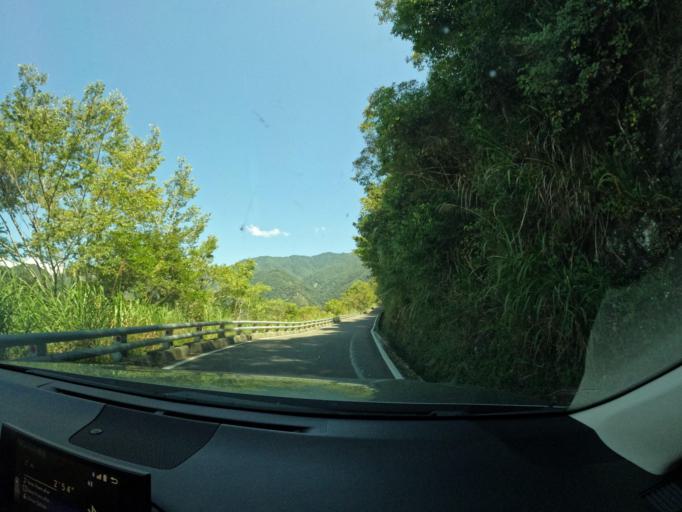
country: TW
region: Taiwan
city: Yujing
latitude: 23.2873
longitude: 120.8498
